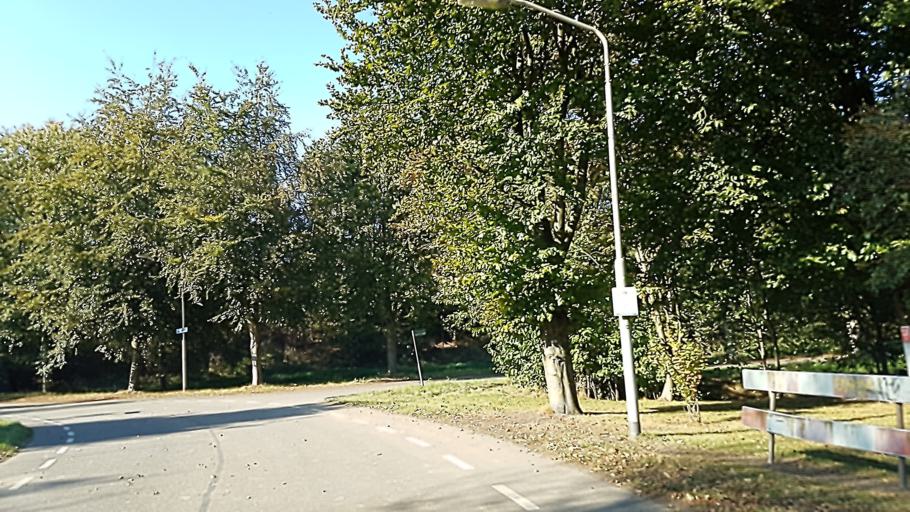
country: NL
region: North Brabant
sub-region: Gemeente Woensdrecht
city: Woensdrecht
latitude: 51.4425
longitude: 4.3150
